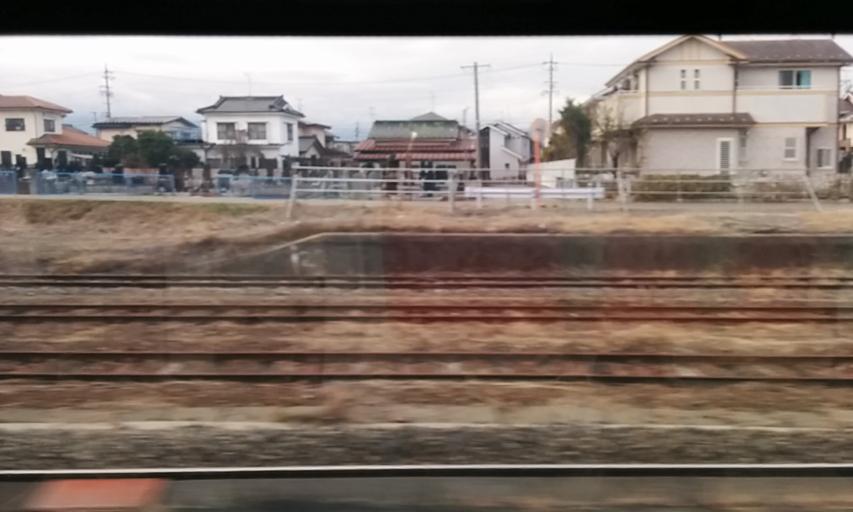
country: JP
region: Nagano
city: Matsumoto
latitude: 36.1734
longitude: 137.9557
